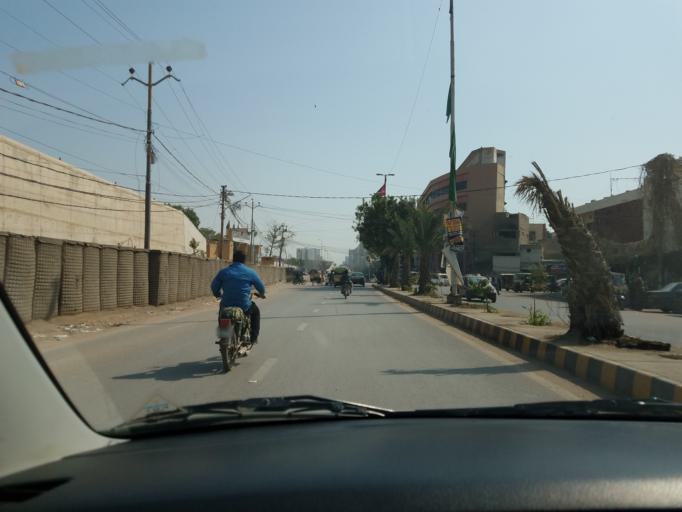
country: PK
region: Sindh
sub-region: Karachi District
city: Karachi
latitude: 24.8876
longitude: 67.0524
